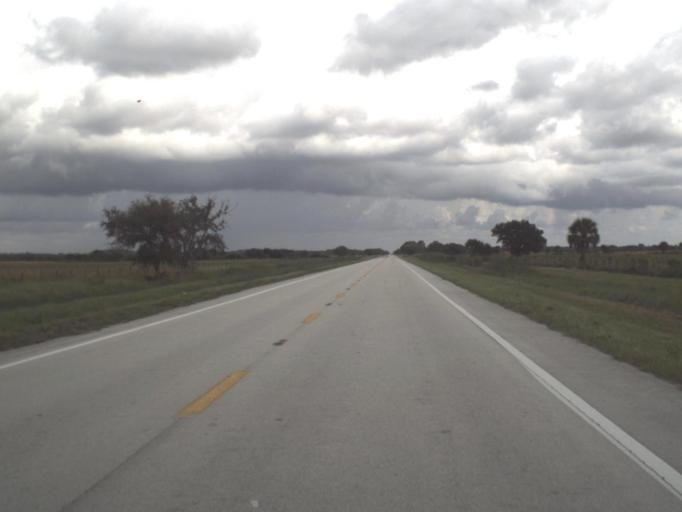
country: US
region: Florida
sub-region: Hendry County
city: Port LaBelle
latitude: 26.8439
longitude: -81.3857
